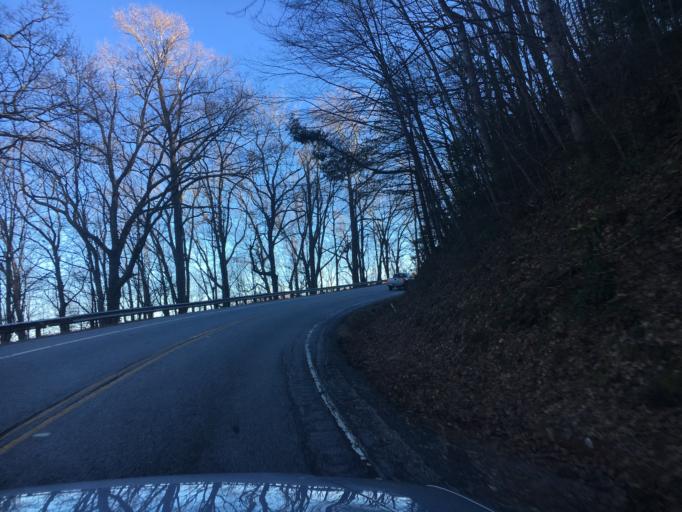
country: US
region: Georgia
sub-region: Union County
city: Blairsville
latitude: 34.7491
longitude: -83.9201
